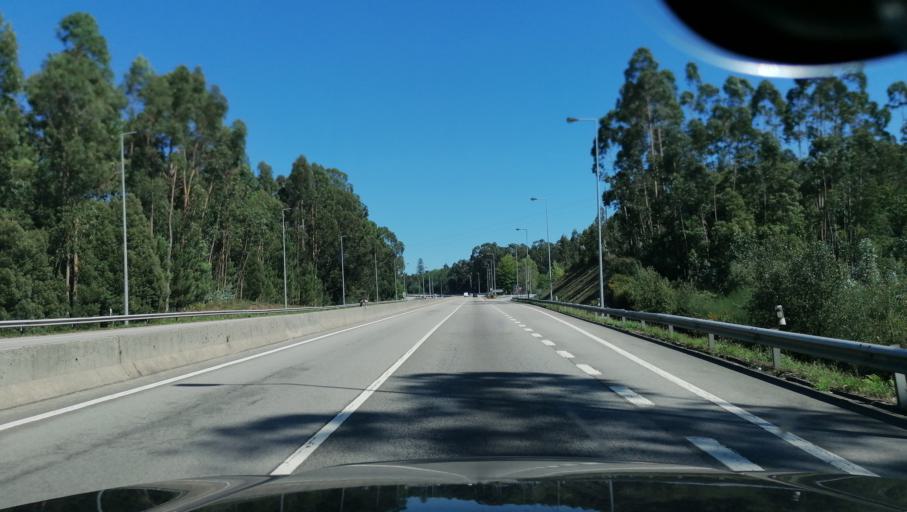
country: PT
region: Aveiro
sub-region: Santa Maria da Feira
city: Rio Meao
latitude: 40.9258
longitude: -8.5831
